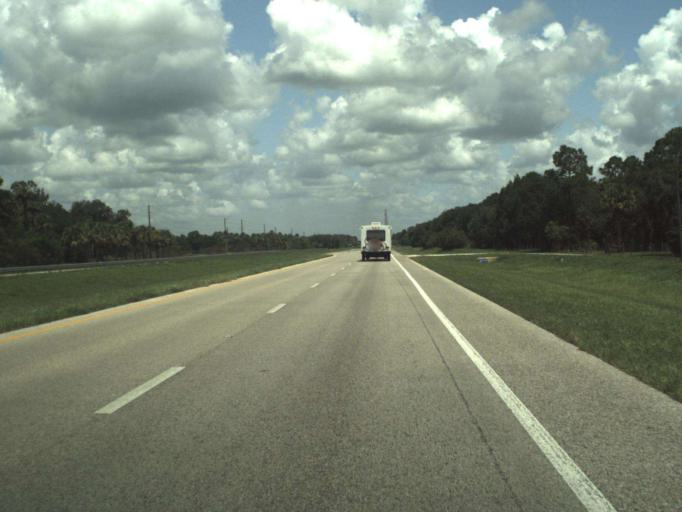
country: US
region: Florida
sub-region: Indian River County
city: Fellsmere
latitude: 27.6561
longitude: -80.7877
